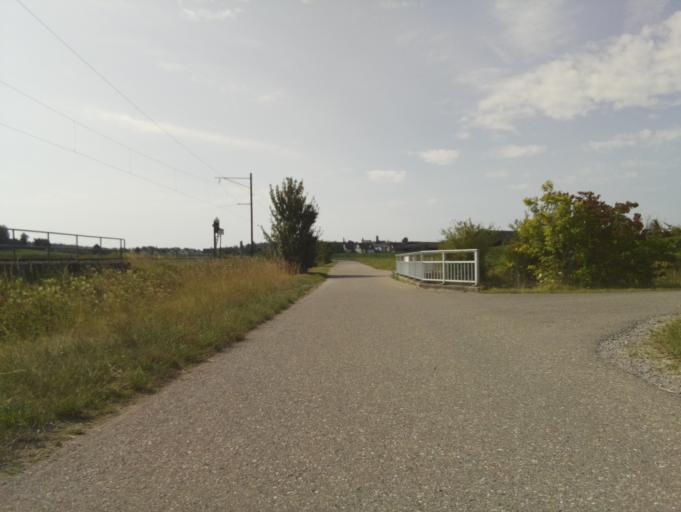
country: CH
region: Zurich
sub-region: Bezirk Andelfingen
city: Henggart
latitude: 47.5712
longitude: 8.6824
